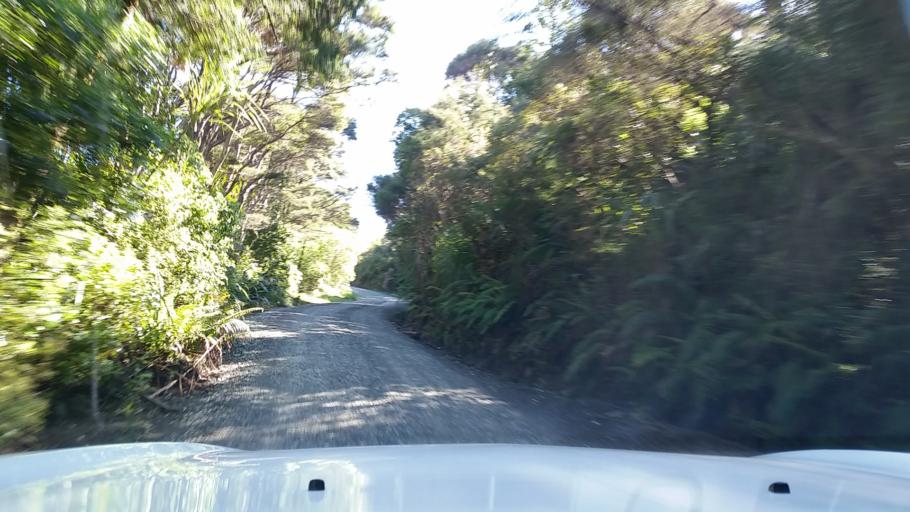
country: NZ
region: Auckland
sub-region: Auckland
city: Titirangi
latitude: -37.0158
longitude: 174.5372
